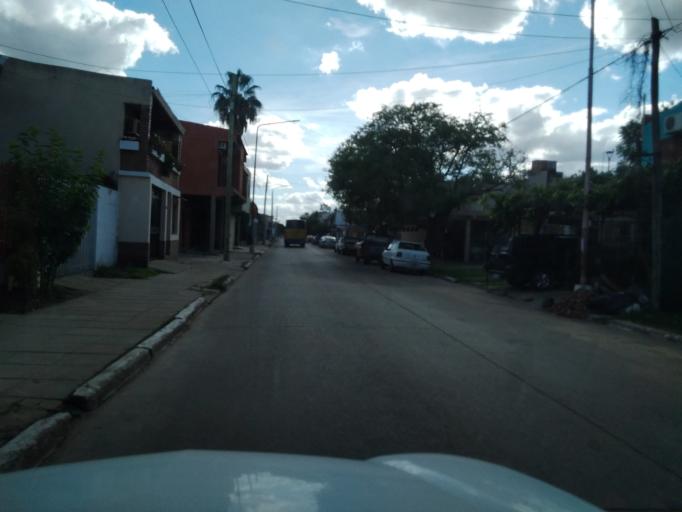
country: AR
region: Corrientes
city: Corrientes
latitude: -27.4966
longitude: -58.8308
